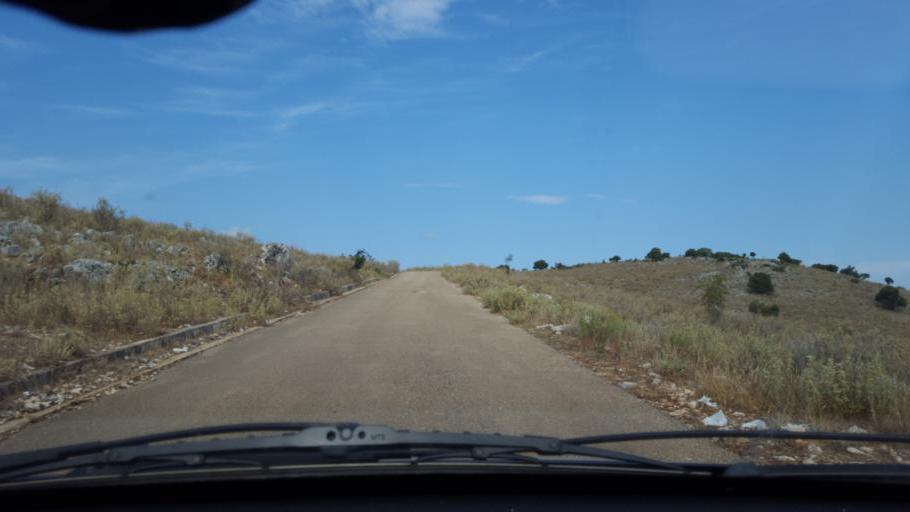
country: AL
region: Vlore
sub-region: Rrethi i Sarandes
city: Xarre
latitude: 39.7590
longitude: 19.9897
